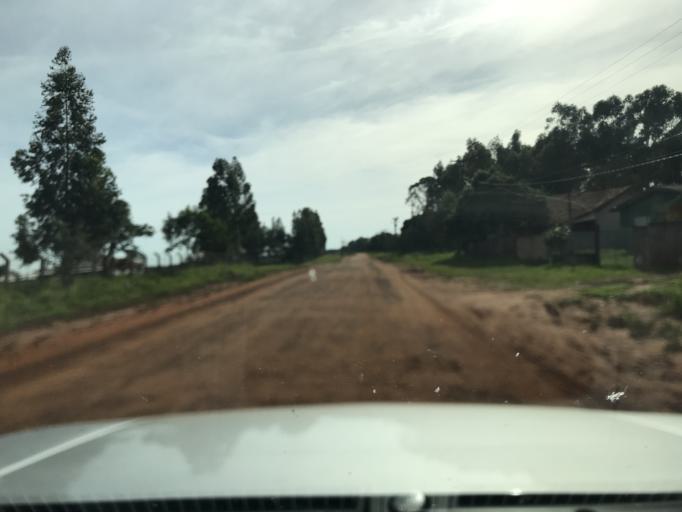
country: BR
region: Mato Grosso do Sul
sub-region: Iguatemi
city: Iguatemi
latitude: -23.6619
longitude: -54.5690
